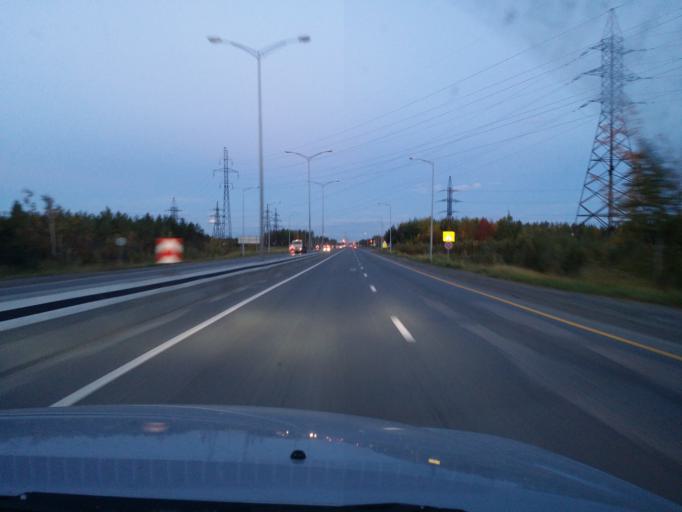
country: RU
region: Khanty-Mansiyskiy Avtonomnyy Okrug
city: Nizhnevartovsk
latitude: 60.9862
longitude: 76.4727
